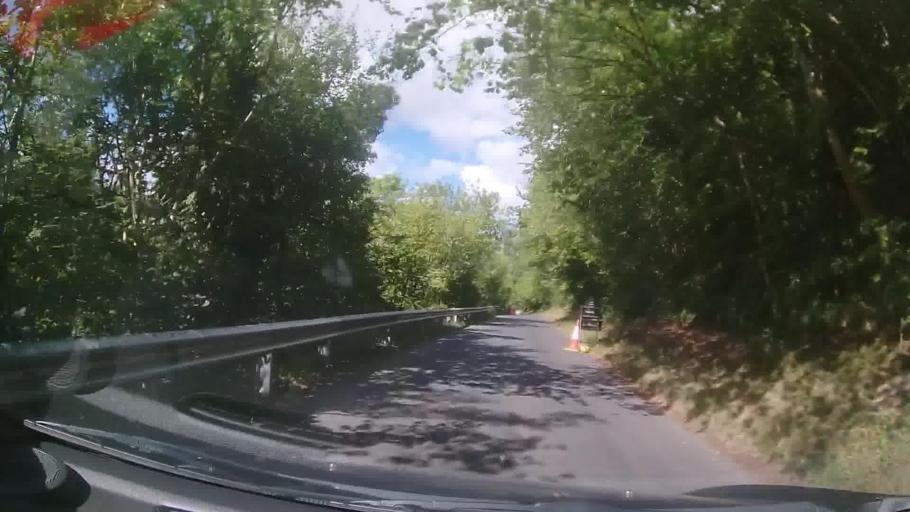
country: GB
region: Wales
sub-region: Merthyr Tydfil County Borough
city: Merthyr Tydfil
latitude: 51.7868
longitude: -3.3632
